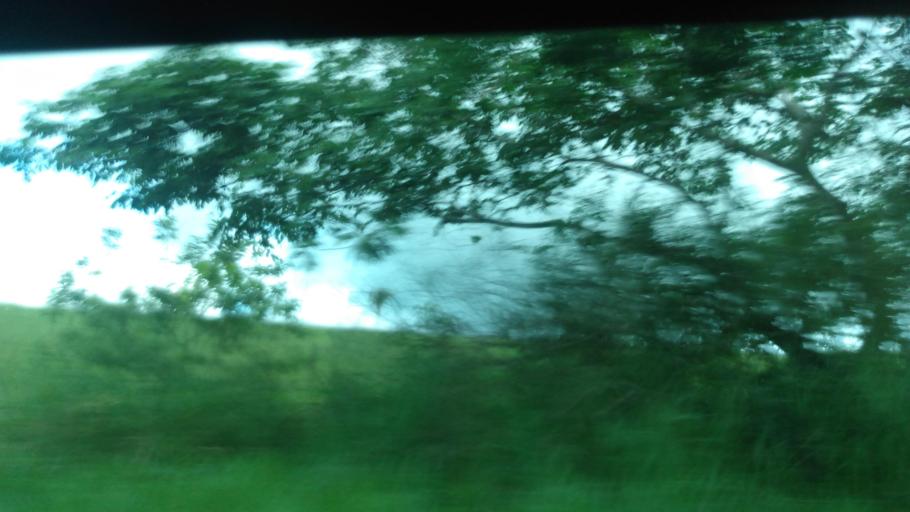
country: BR
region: Pernambuco
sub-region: Quipapa
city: Quipapa
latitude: -8.7917
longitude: -35.9850
